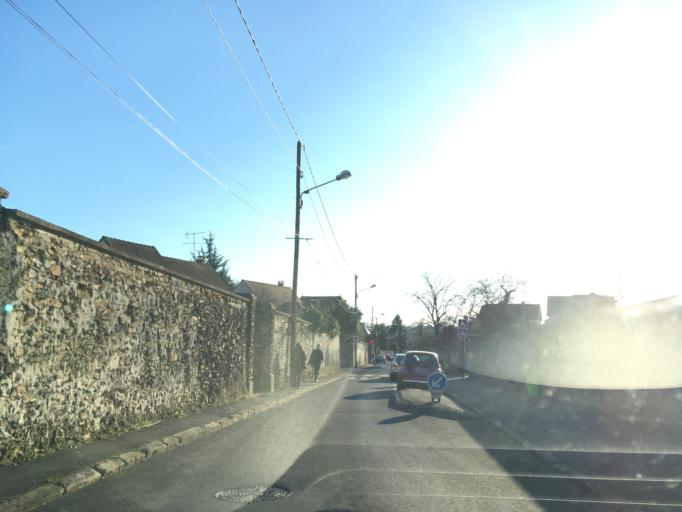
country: FR
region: Ile-de-France
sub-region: Departement de l'Essonne
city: Epinay-sous-Senart
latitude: 48.7032
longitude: 2.5081
